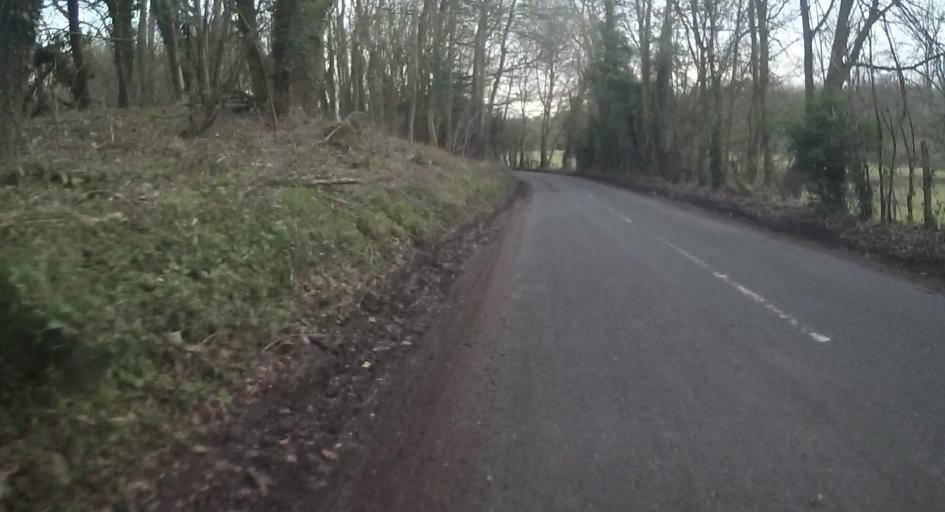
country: GB
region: England
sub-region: Hampshire
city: Highclere
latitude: 51.2261
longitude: -1.3793
